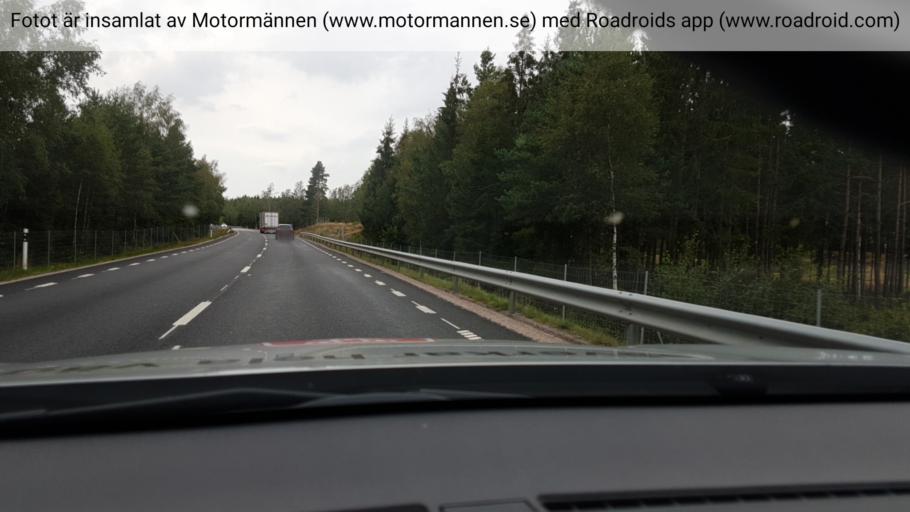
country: SE
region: Vaestra Goetaland
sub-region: Tranemo Kommun
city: Langhem
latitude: 57.5992
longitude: 13.1768
